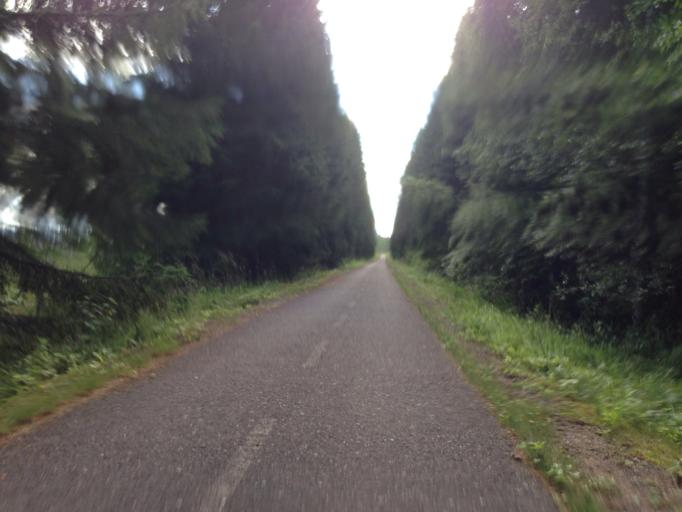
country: SE
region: Dalarna
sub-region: Ludvika Kommun
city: Ludvika
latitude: 60.2030
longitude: 15.1016
